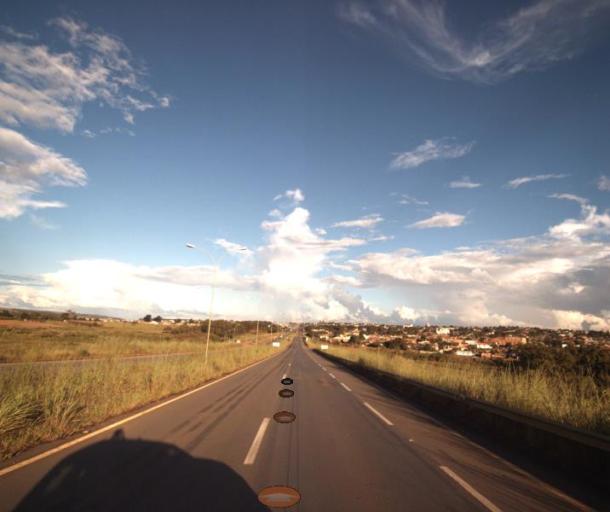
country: BR
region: Goias
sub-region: Anapolis
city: Anapolis
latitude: -16.2704
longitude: -48.9760
